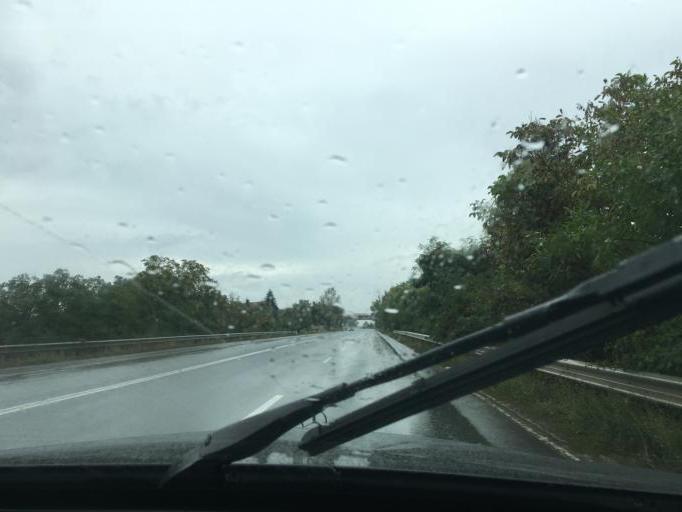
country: BG
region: Sofiya
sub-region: Obshtina Bozhurishte
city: Bozhurishte
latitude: 42.7935
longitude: 23.1484
